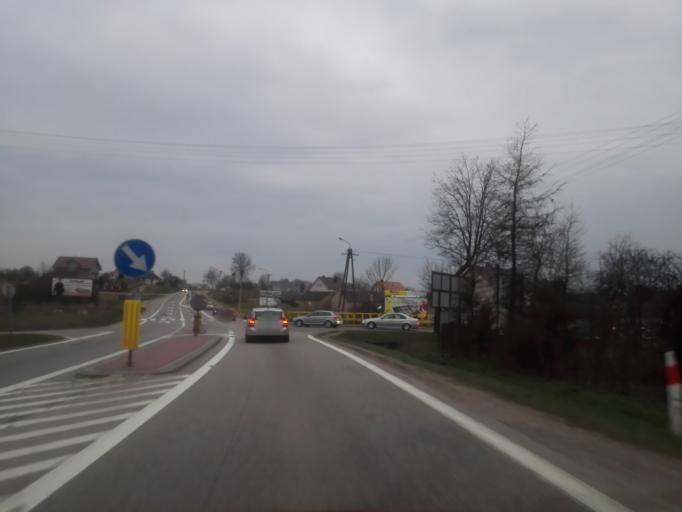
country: PL
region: Podlasie
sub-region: Powiat lomzynski
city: Piatnica
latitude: 53.2547
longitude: 22.1215
